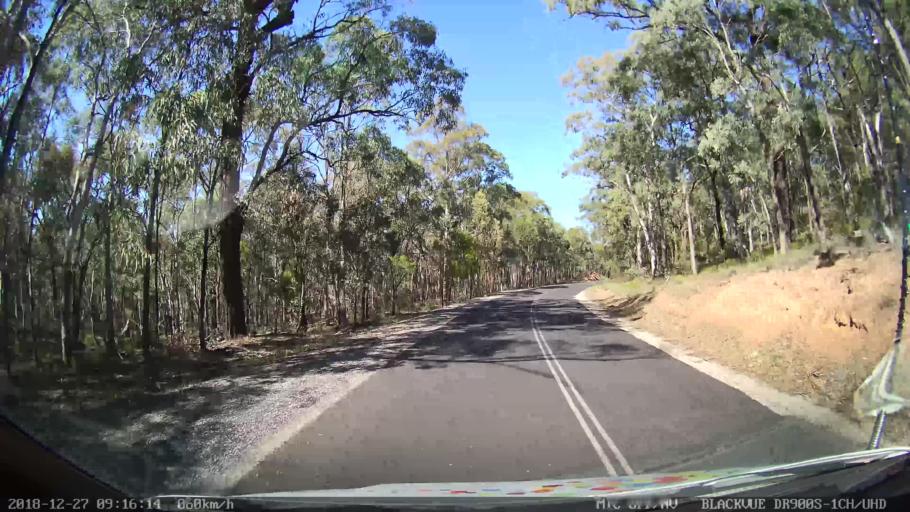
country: AU
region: New South Wales
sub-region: Lithgow
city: Portland
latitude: -33.1371
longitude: 150.0642
